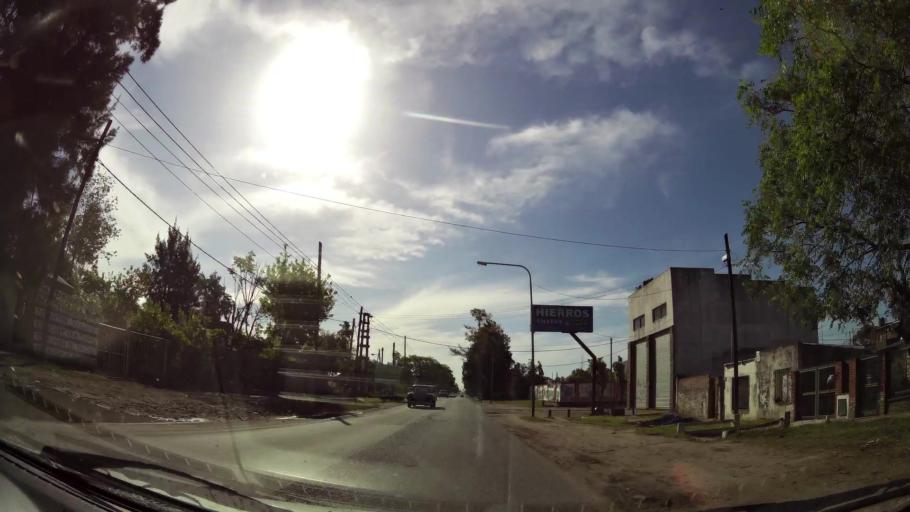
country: AR
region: Buenos Aires
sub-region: Partido de Quilmes
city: Quilmes
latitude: -34.7998
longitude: -58.2276
